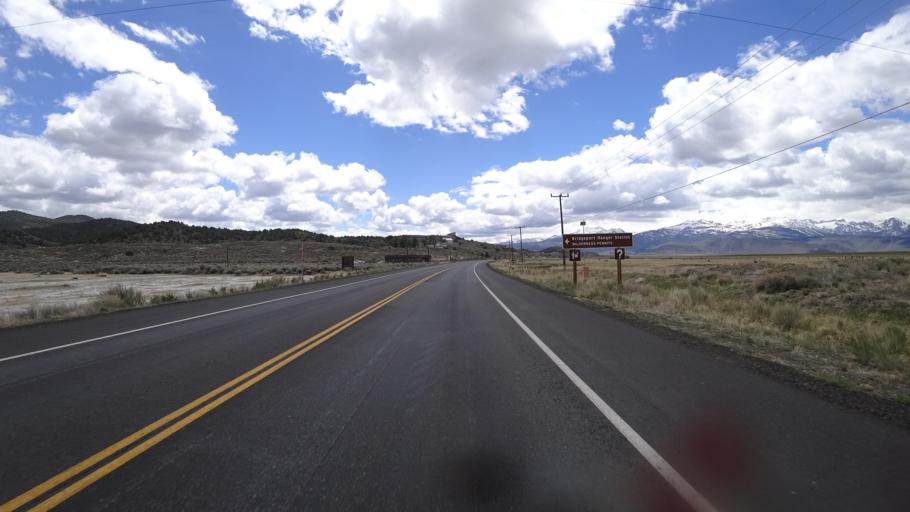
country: US
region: California
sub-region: Mono County
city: Bridgeport
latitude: 38.2489
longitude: -119.2210
